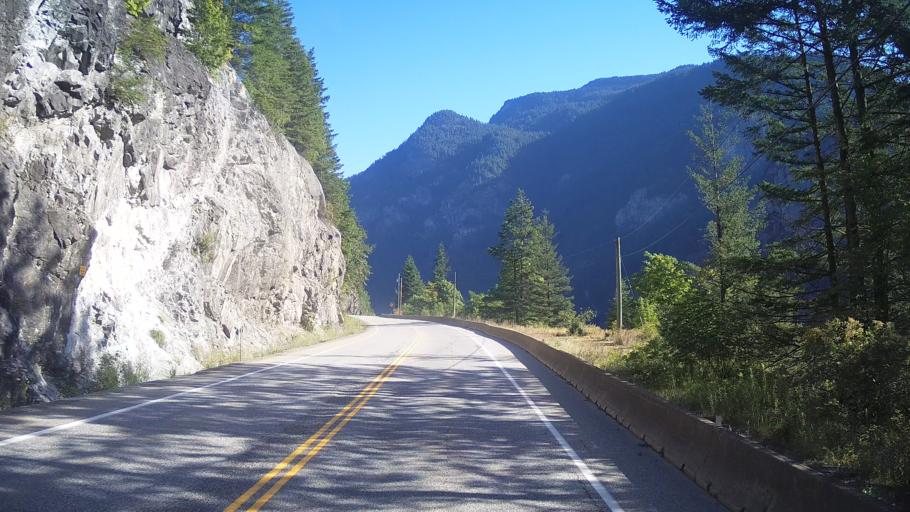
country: CA
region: British Columbia
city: Hope
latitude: 49.5725
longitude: -121.4038
